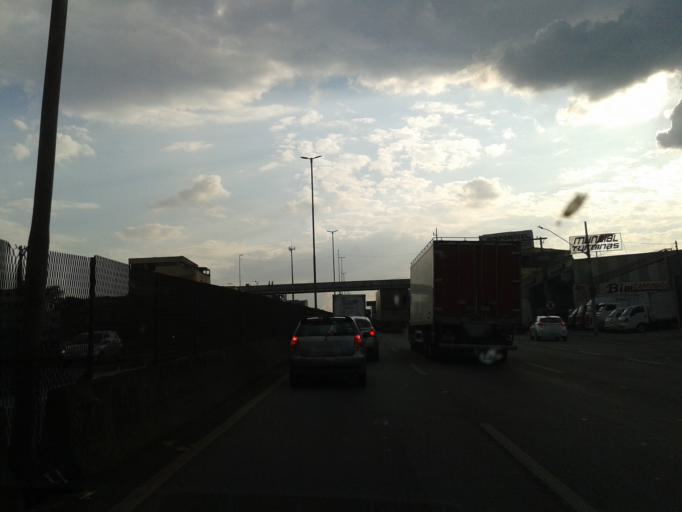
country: BR
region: Minas Gerais
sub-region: Contagem
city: Contagem
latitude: -19.9612
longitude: -44.0373
